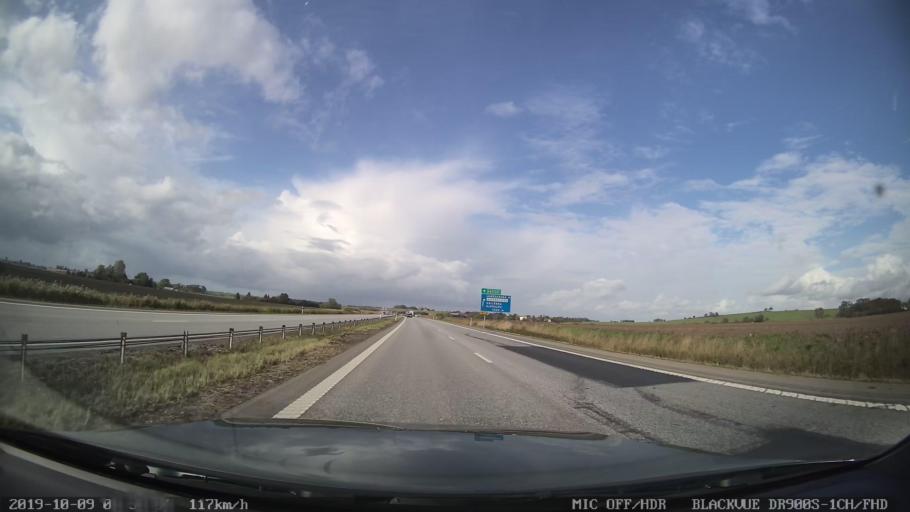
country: SE
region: Skane
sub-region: Landskrona
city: Landskrona
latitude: 55.9143
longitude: 12.8532
